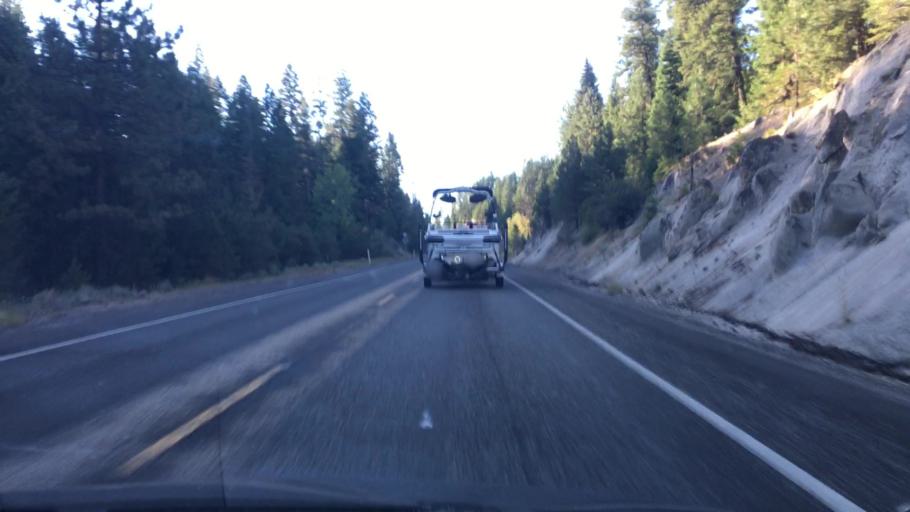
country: US
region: Idaho
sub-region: Valley County
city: Cascade
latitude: 44.5748
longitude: -116.0332
